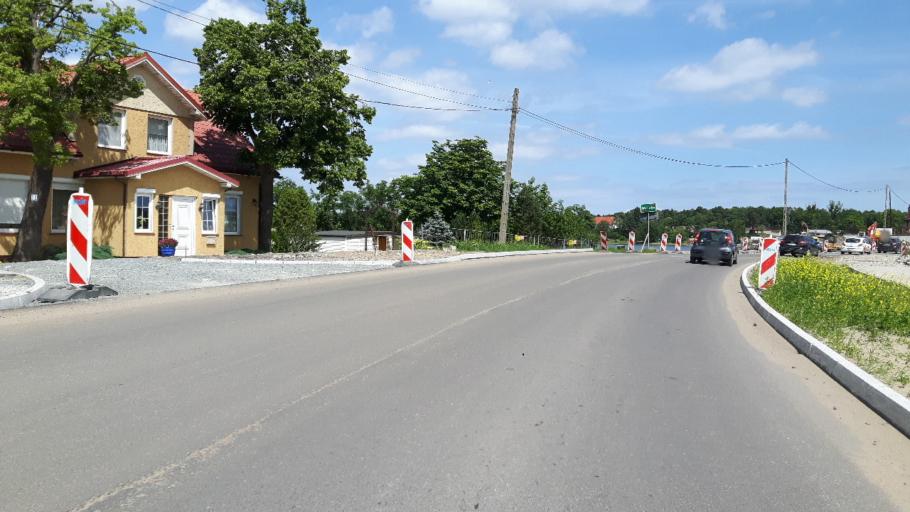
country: PL
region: Pomeranian Voivodeship
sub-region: Powiat gdanski
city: Cedry Wielkie
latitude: 54.3403
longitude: 18.8234
